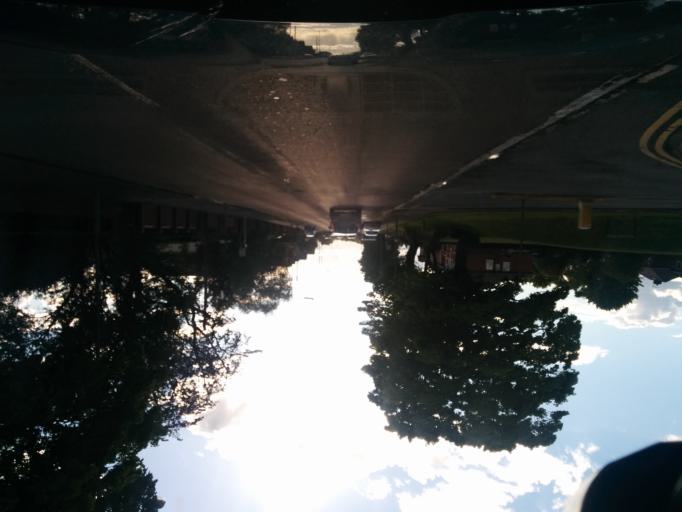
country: GB
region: England
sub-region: Northumberland
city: Cramlington
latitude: 55.0871
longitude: -1.5873
